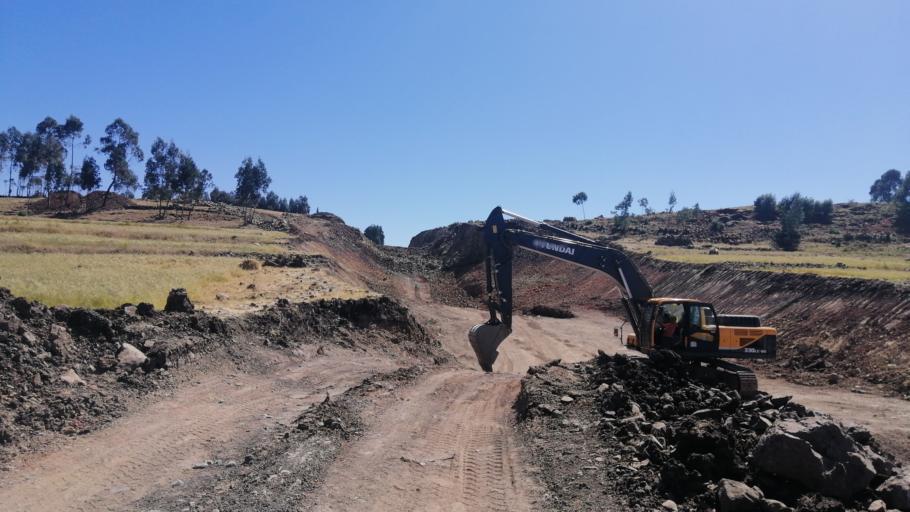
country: ET
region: Amhara
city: Debre Tabor
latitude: 11.4204
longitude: 38.2148
